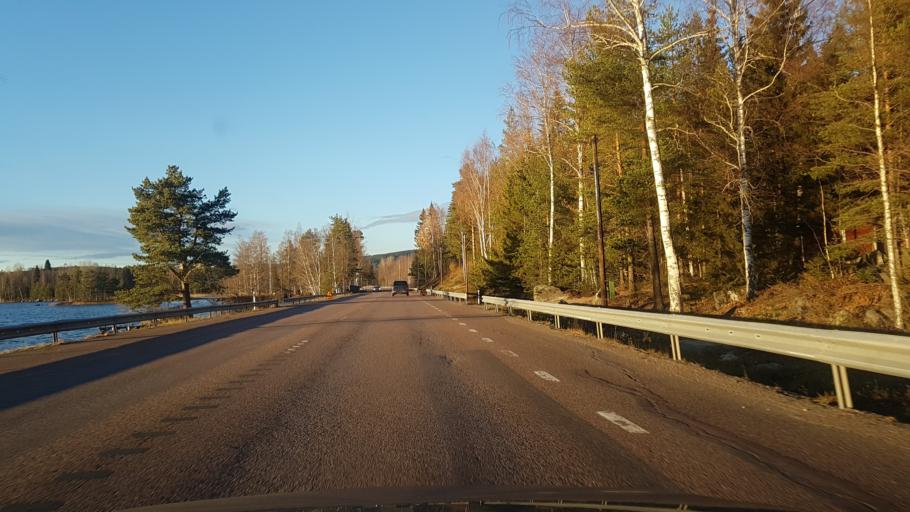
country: SE
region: Dalarna
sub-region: Faluns Kommun
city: Bjursas
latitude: 60.7149
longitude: 15.4600
